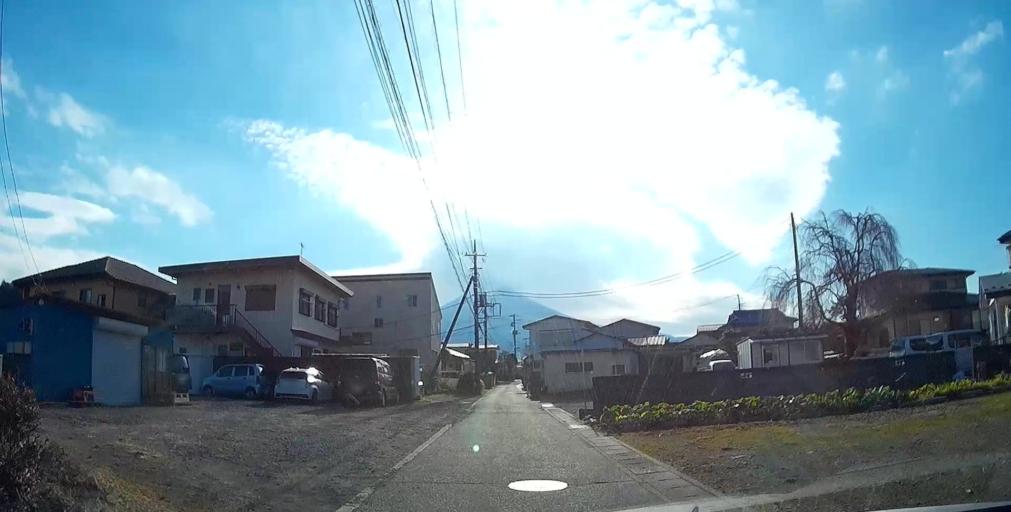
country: JP
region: Yamanashi
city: Fujikawaguchiko
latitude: 35.4944
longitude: 138.8218
